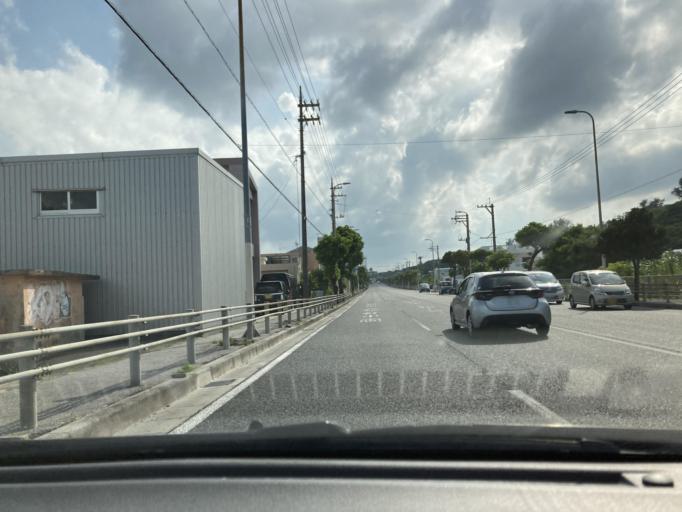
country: JP
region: Okinawa
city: Ginowan
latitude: 26.2446
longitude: 127.7810
